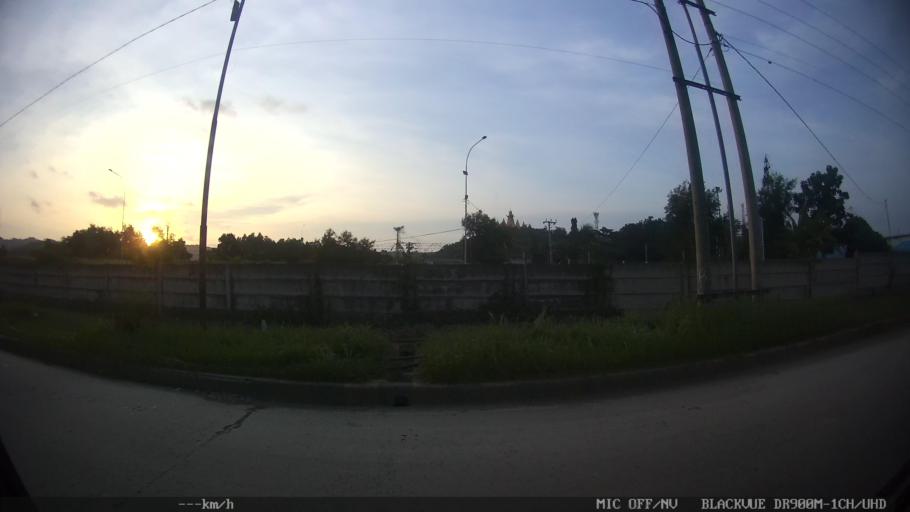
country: ID
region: Lampung
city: Penengahan
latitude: -5.8693
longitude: 105.7531
